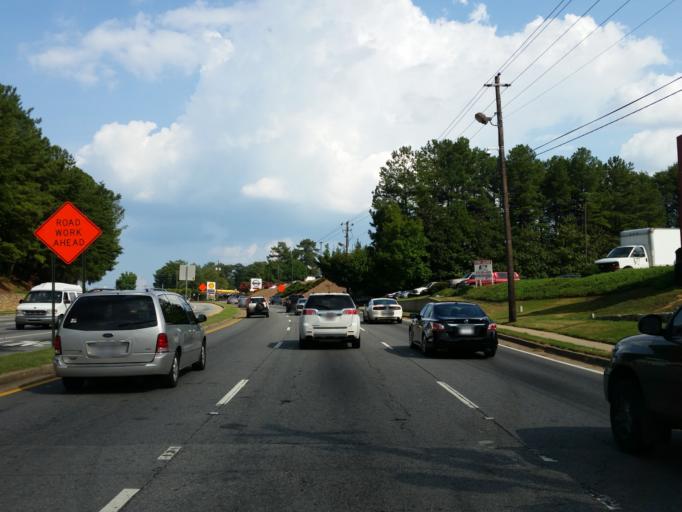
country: US
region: Georgia
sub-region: Fulton County
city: Roswell
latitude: 34.0235
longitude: -84.3295
